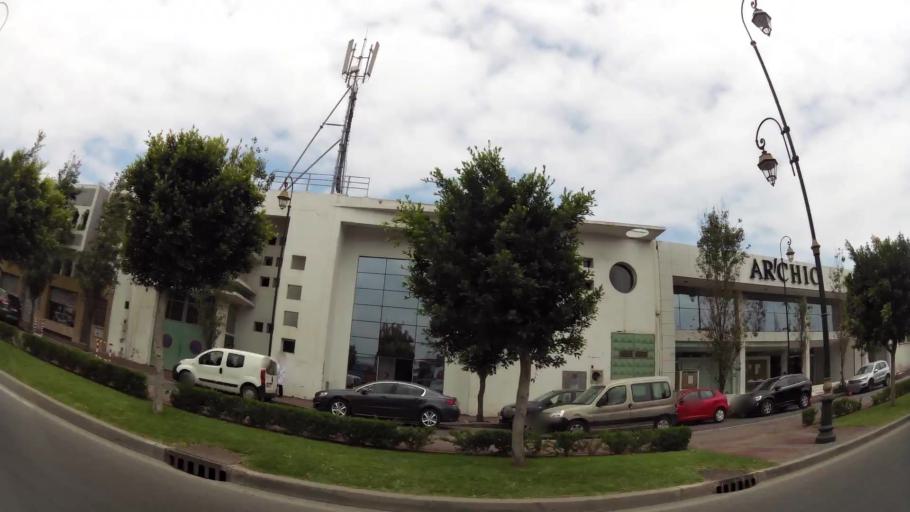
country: MA
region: Rabat-Sale-Zemmour-Zaer
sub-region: Rabat
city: Rabat
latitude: 33.9840
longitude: -6.8715
